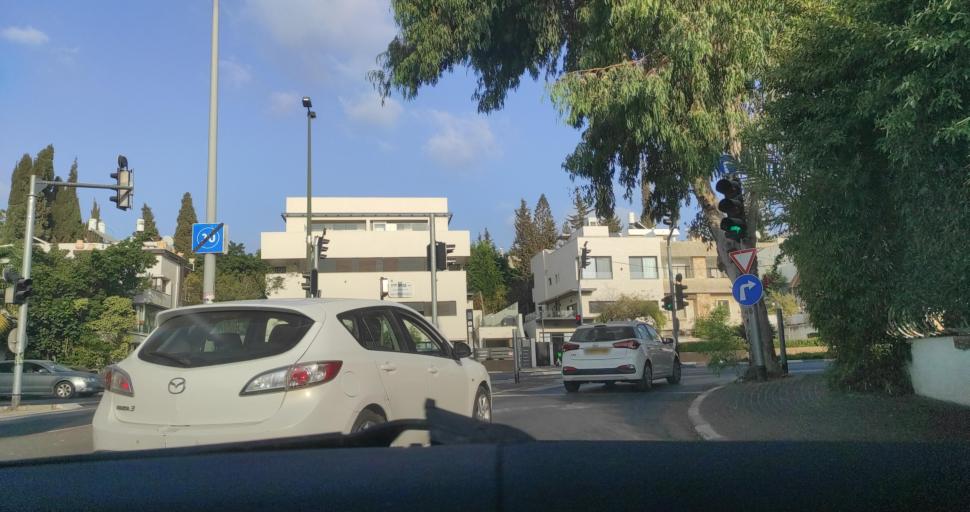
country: IL
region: Tel Aviv
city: Bene Beraq
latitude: 32.1123
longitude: 34.8247
